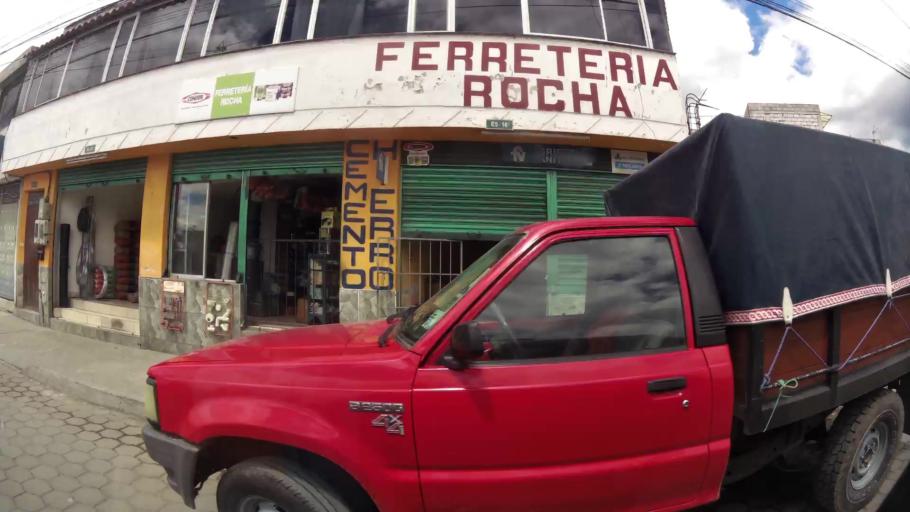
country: EC
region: Pichincha
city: Sangolqui
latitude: -0.3351
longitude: -78.5370
